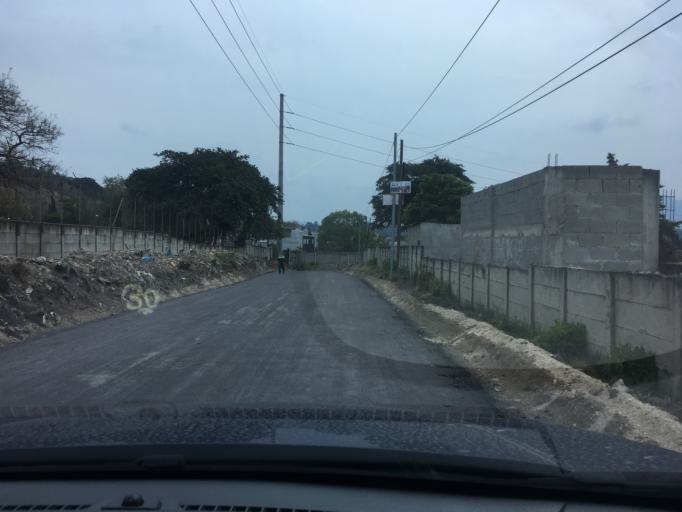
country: GT
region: Guatemala
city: Petapa
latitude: 14.5142
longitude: -90.5535
